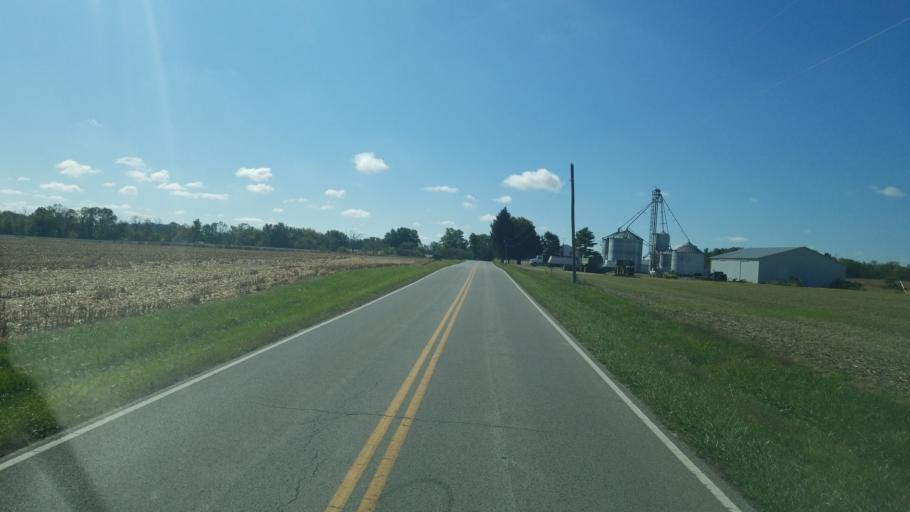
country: US
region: Ohio
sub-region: Highland County
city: Leesburg
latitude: 39.2950
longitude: -83.5797
